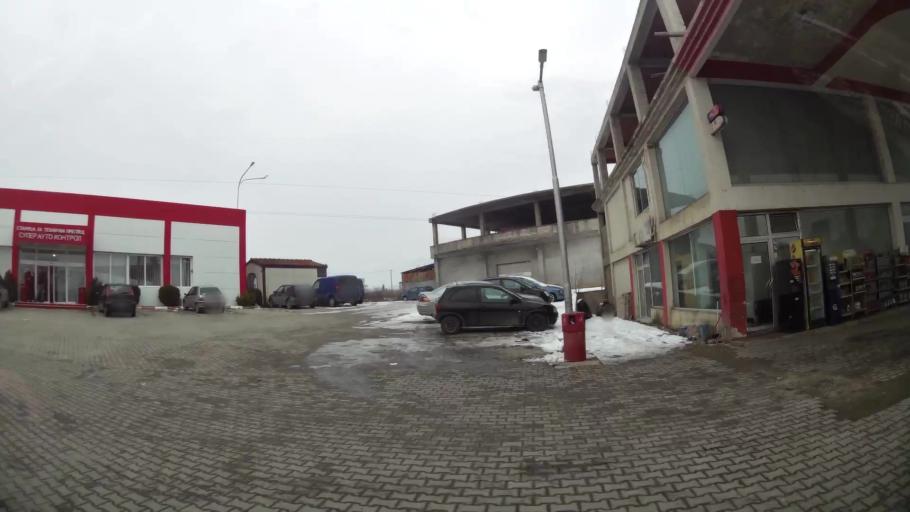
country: MK
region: Suto Orizari
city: Suto Orizare
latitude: 42.0476
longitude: 21.4299
